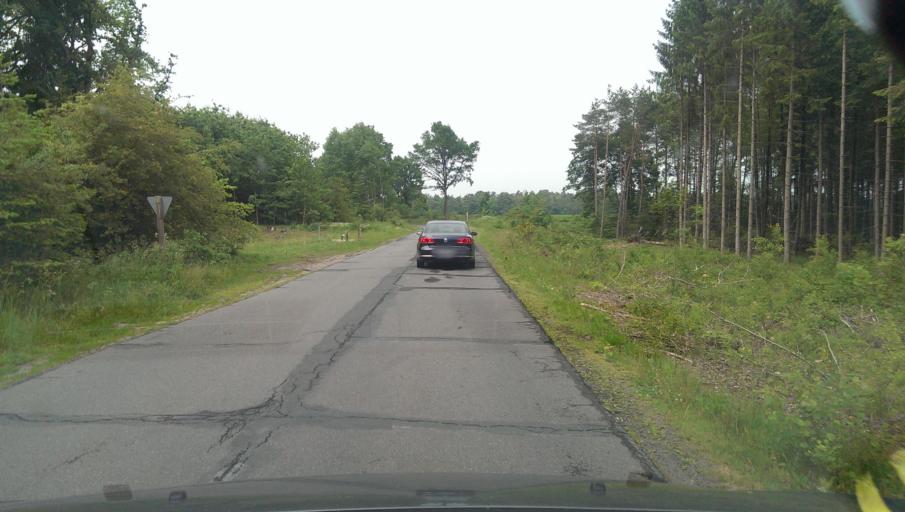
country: DE
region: Lower Saxony
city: Fassberg
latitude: 52.8904
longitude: 10.1644
